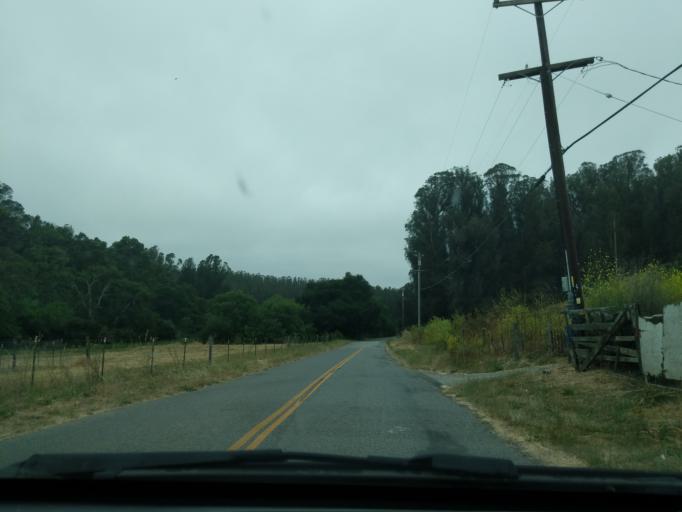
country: US
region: California
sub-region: San Benito County
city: Aromas
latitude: 36.8880
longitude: -121.5974
